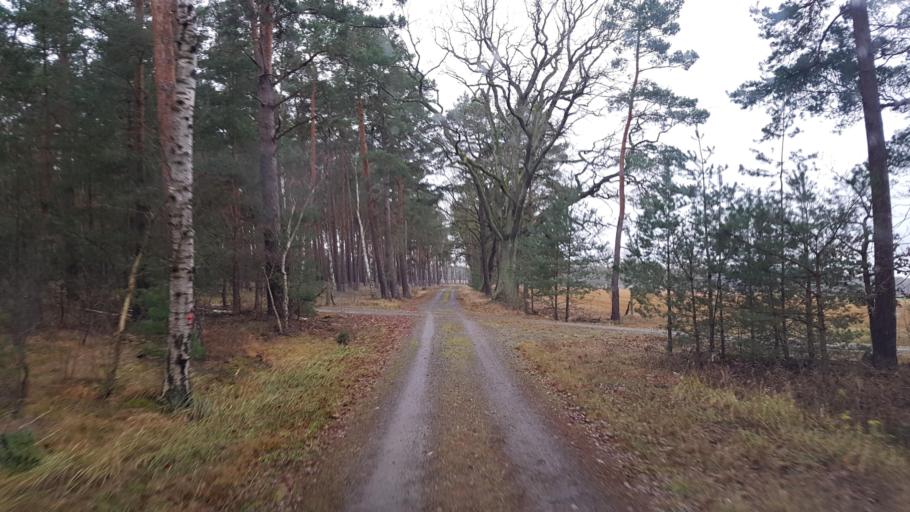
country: DE
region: Brandenburg
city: Tauche
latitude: 52.0917
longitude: 14.1077
